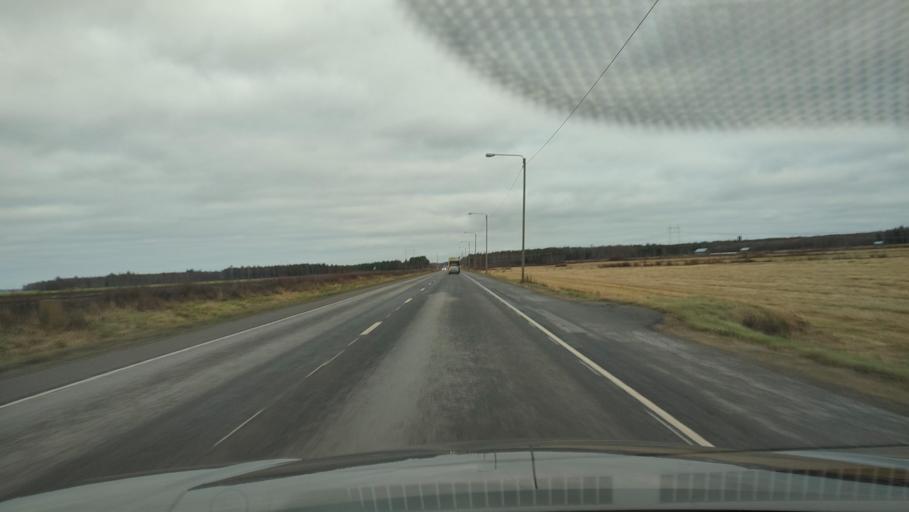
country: FI
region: Southern Ostrobothnia
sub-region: Seinaejoki
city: Ilmajoki
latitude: 62.7413
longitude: 22.6207
